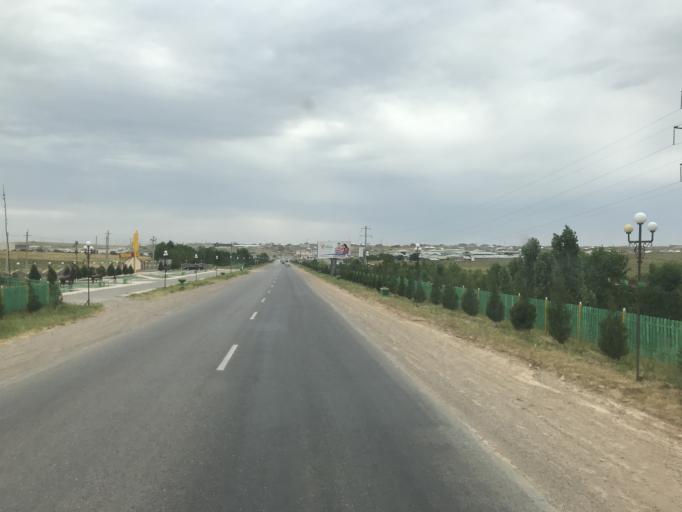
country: KZ
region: Ongtustik Qazaqstan
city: Saryaghash
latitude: 41.4765
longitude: 69.2178
